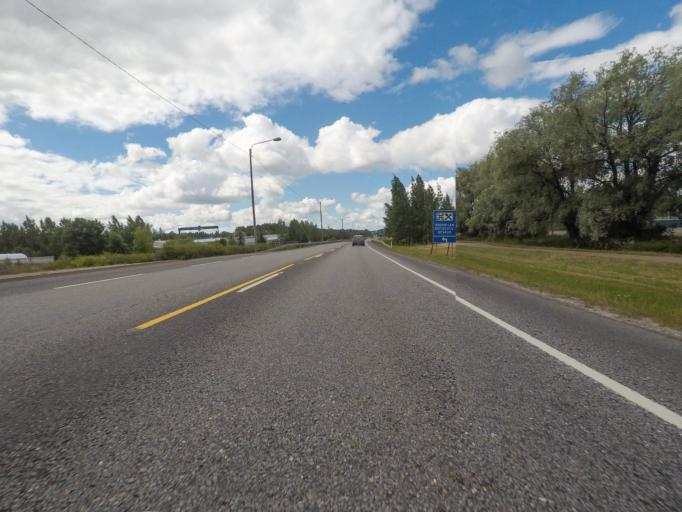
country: FI
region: Varsinais-Suomi
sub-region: Turku
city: Raisio
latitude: 60.4728
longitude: 22.1479
